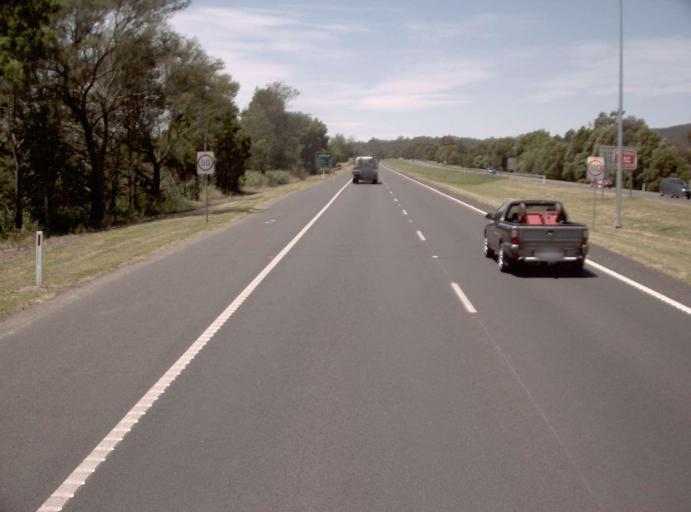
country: AU
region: Victoria
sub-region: Latrobe
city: Moe
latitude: -38.2057
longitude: 146.1671
